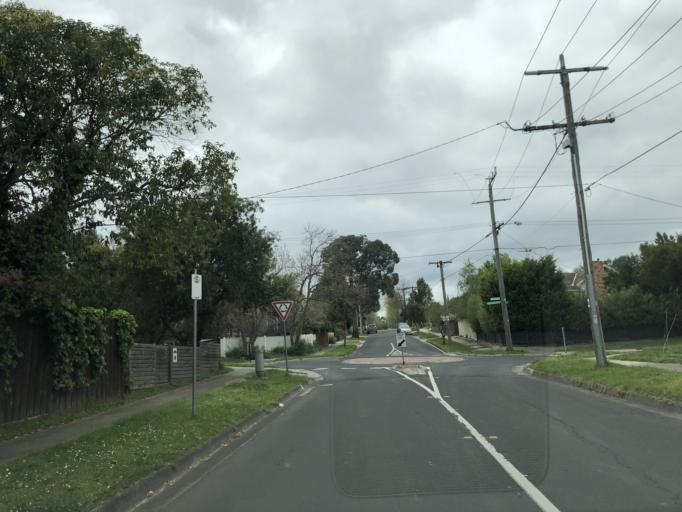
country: AU
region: Victoria
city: Burwood East
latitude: -37.8396
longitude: 145.1393
